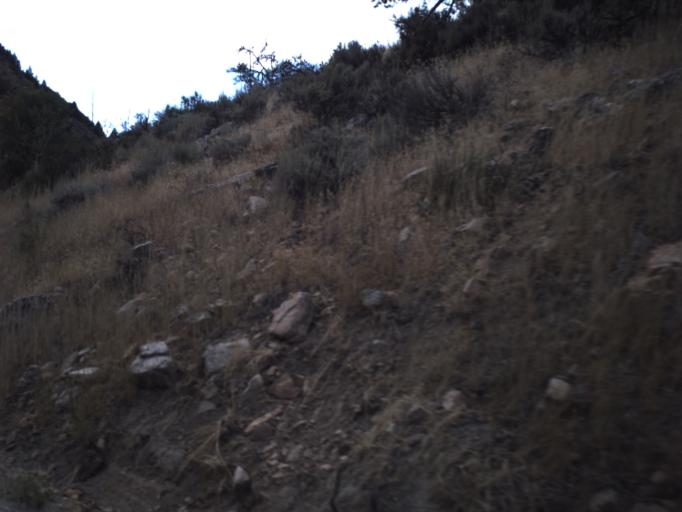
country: US
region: Utah
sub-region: Cache County
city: Millville
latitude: 41.6053
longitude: -111.5974
